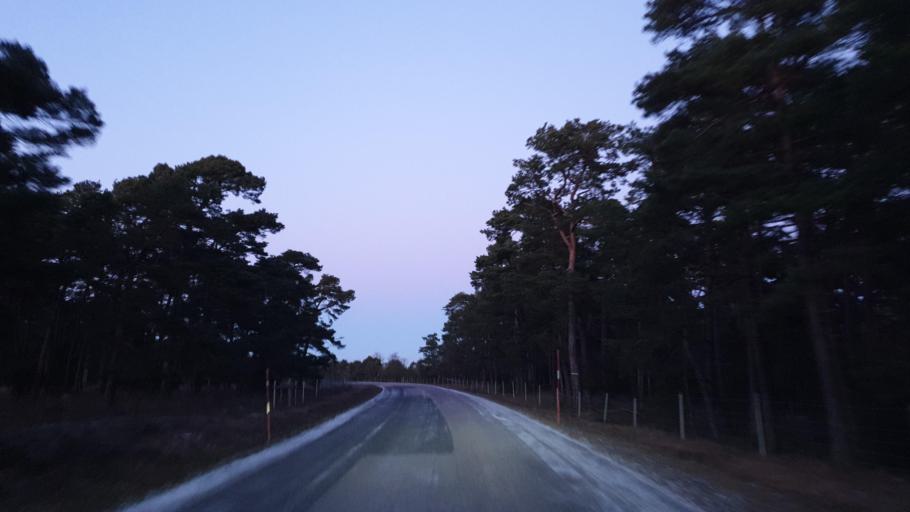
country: SE
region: Gotland
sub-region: Gotland
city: Slite
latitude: 57.4149
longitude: 18.8133
